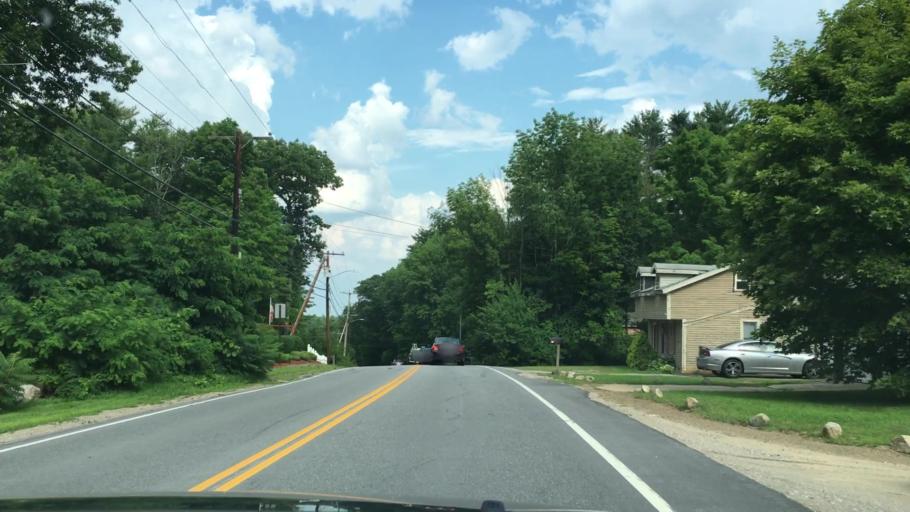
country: US
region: New Hampshire
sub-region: Belknap County
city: Gilford
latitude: 43.6019
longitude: -71.4464
